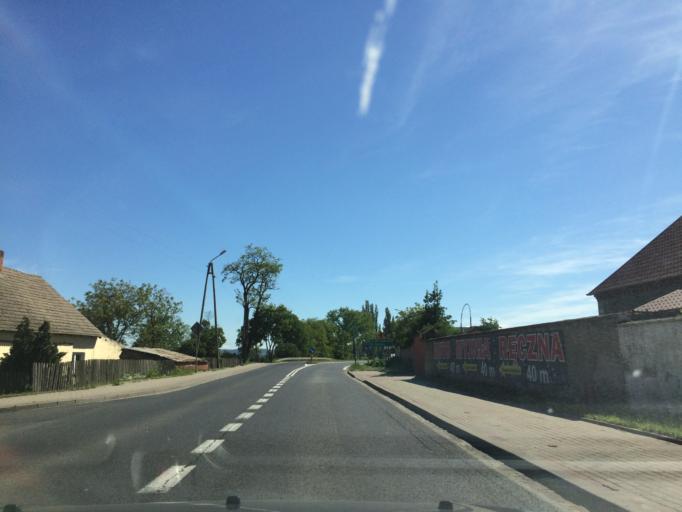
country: PL
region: Lower Silesian Voivodeship
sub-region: Powiat wroclawski
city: Gniechowice
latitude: 50.9547
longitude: 16.7817
